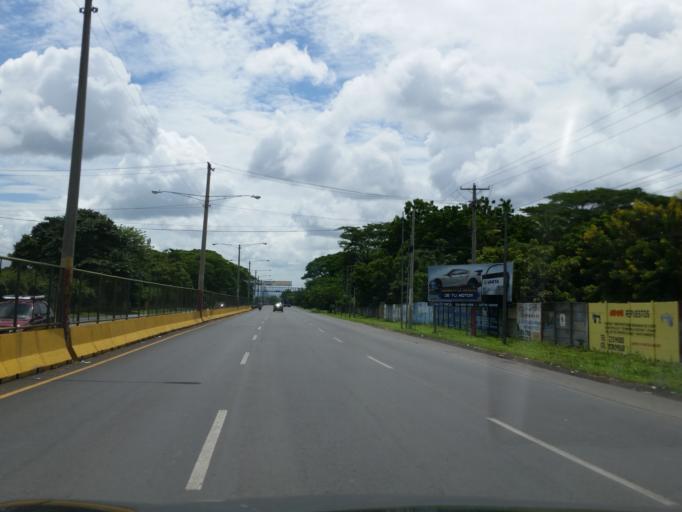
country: NI
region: Managua
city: Tipitapa
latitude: 12.1484
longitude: -86.1593
